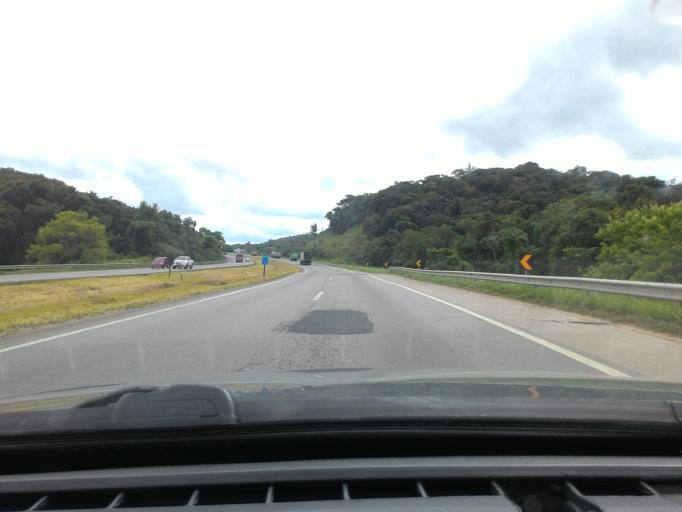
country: BR
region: Sao Paulo
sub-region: Registro
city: Registro
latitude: -24.5631
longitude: -47.8685
